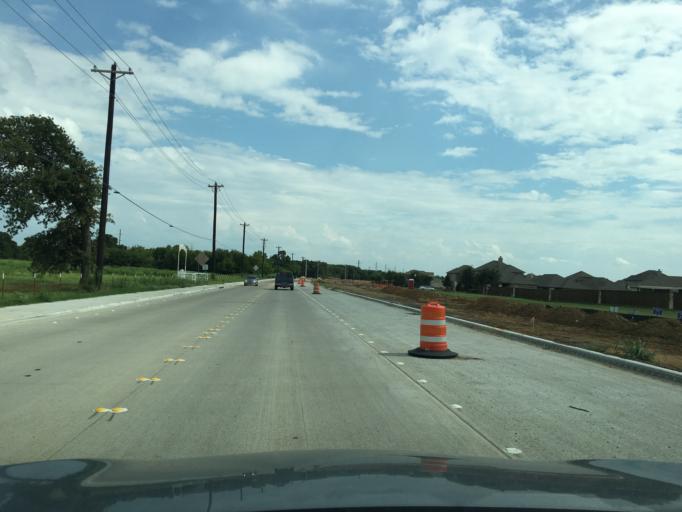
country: US
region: Texas
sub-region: Denton County
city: Oak Point
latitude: 33.2139
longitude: -96.9758
